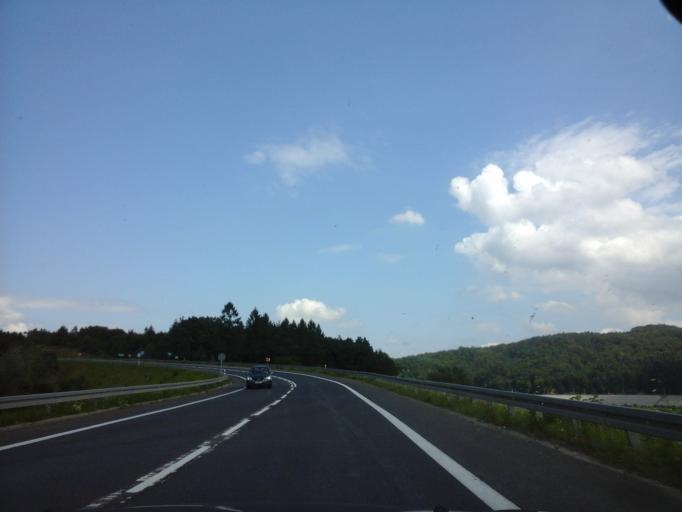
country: PL
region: Lesser Poland Voivodeship
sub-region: Powiat suski
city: Zembrzyce
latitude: 49.7934
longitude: 19.5839
